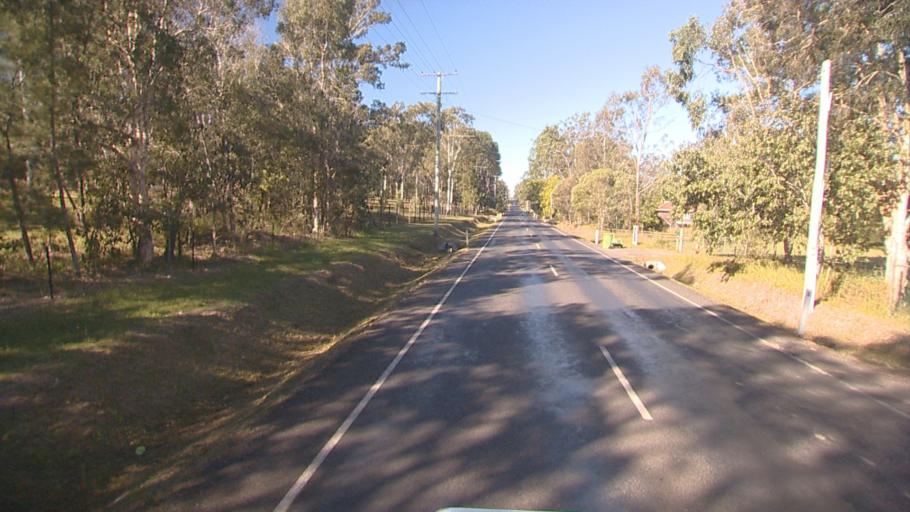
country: AU
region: Queensland
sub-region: Logan
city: Park Ridge South
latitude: -27.7224
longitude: 153.0000
